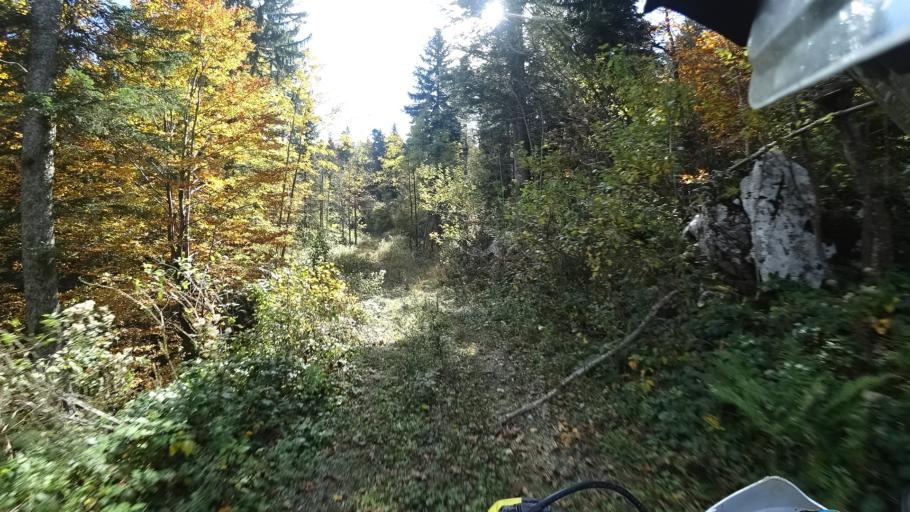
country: HR
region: Karlovacka
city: Plaski
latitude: 45.0603
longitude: 15.3239
